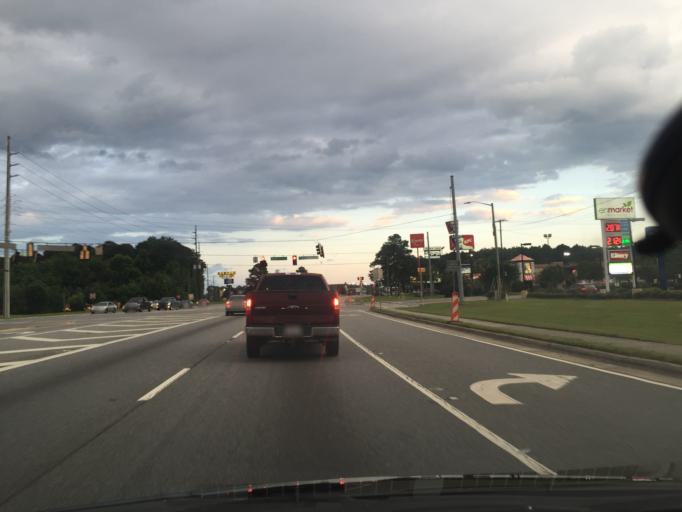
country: US
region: Georgia
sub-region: Chatham County
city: Pooler
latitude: 32.1117
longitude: -81.2357
